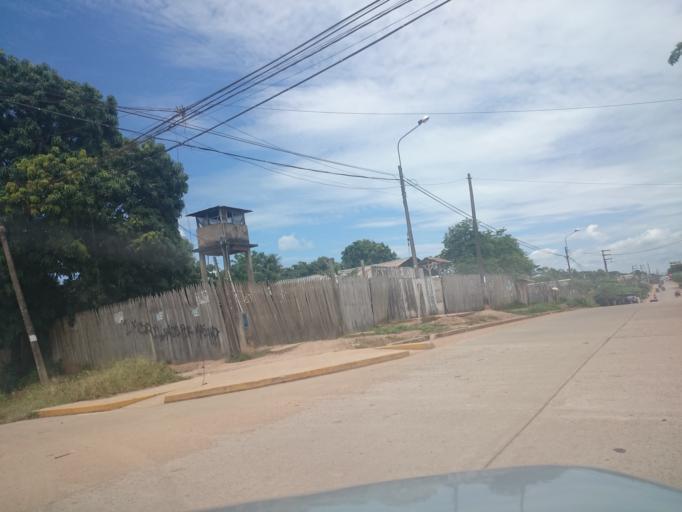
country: PE
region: Ucayali
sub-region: Provincia de Coronel Portillo
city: Puerto Callao
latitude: -8.3565
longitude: -74.5803
